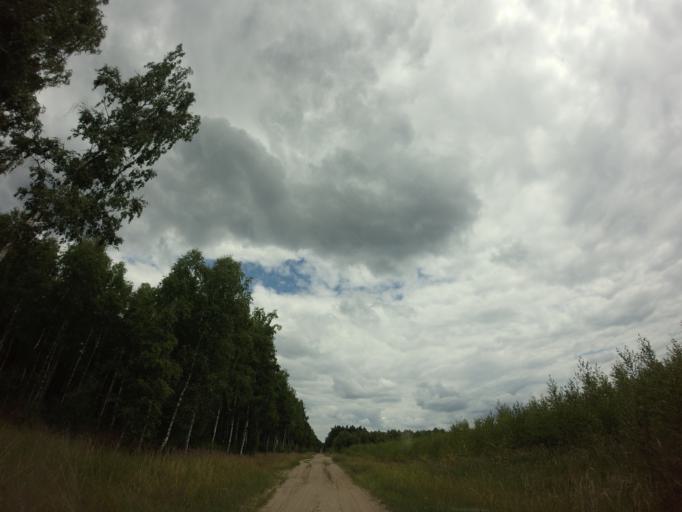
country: PL
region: West Pomeranian Voivodeship
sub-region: Powiat choszczenski
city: Drawno
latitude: 53.1511
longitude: 15.7074
